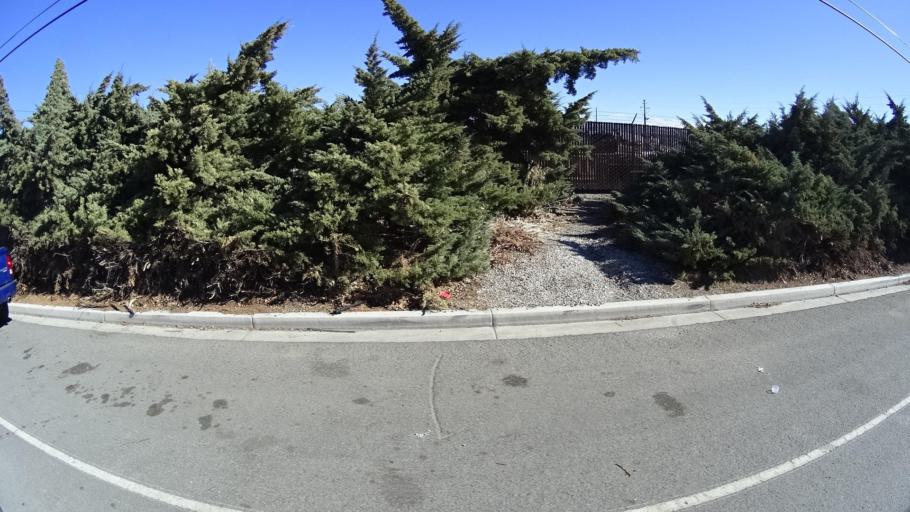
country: US
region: Nevada
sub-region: Washoe County
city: Sparks
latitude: 39.5098
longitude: -119.7559
